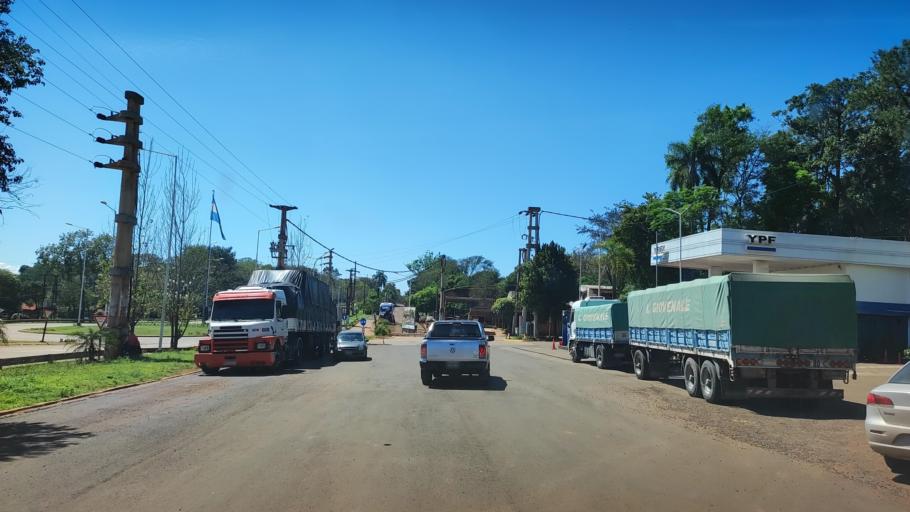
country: AR
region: Misiones
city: Puerto Rico
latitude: -26.8211
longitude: -55.0235
